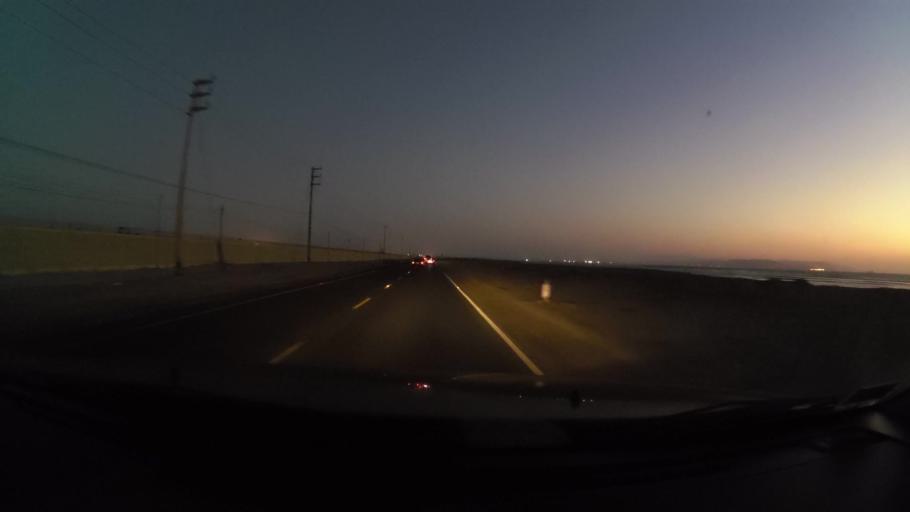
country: PE
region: Ica
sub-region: Provincia de Pisco
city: Pisco
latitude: -13.7531
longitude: -76.2303
